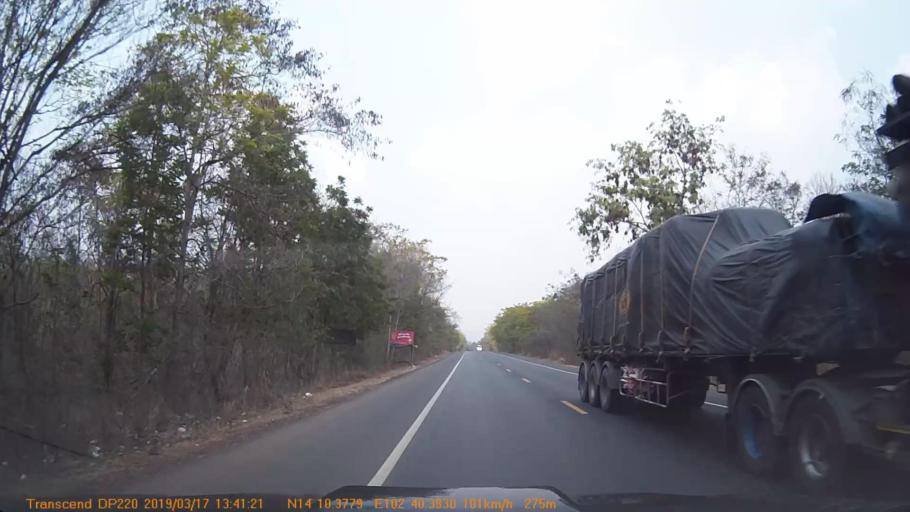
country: TH
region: Buriram
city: Non Din Daeng
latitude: 14.1730
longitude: 102.6733
